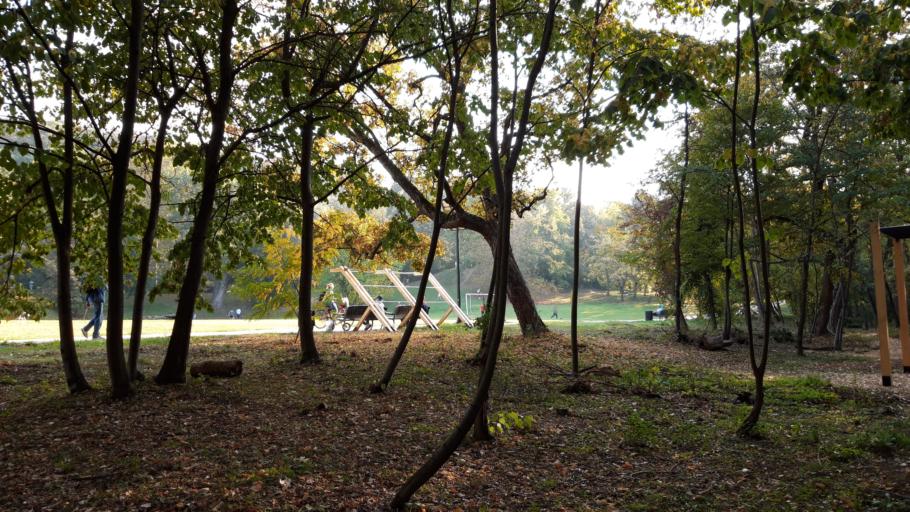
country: RS
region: Autonomna Pokrajina Vojvodina
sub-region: Juznobacki Okrug
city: Novi Sad
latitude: 45.2295
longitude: 19.8492
